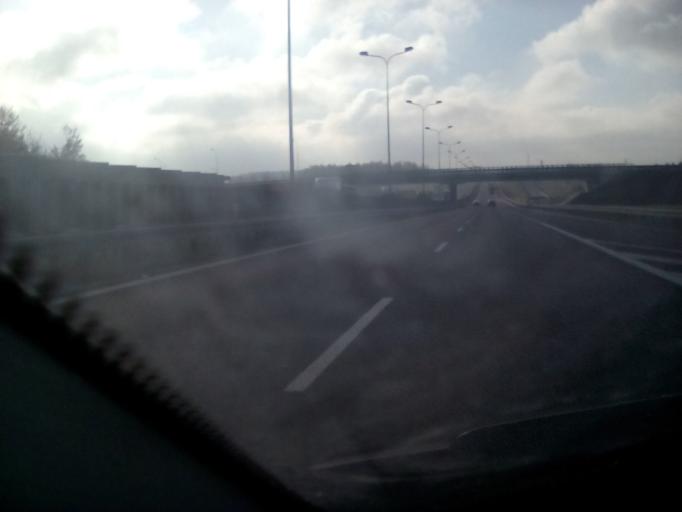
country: PL
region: Masovian Voivodeship
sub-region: Powiat grojecki
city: Goszczyn
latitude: 51.7365
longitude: 20.9142
